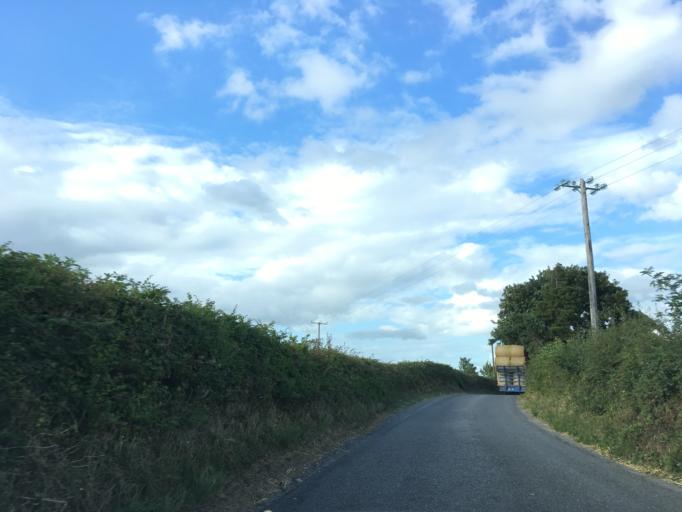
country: IE
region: Munster
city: Cahir
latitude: 52.2964
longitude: -7.9491
